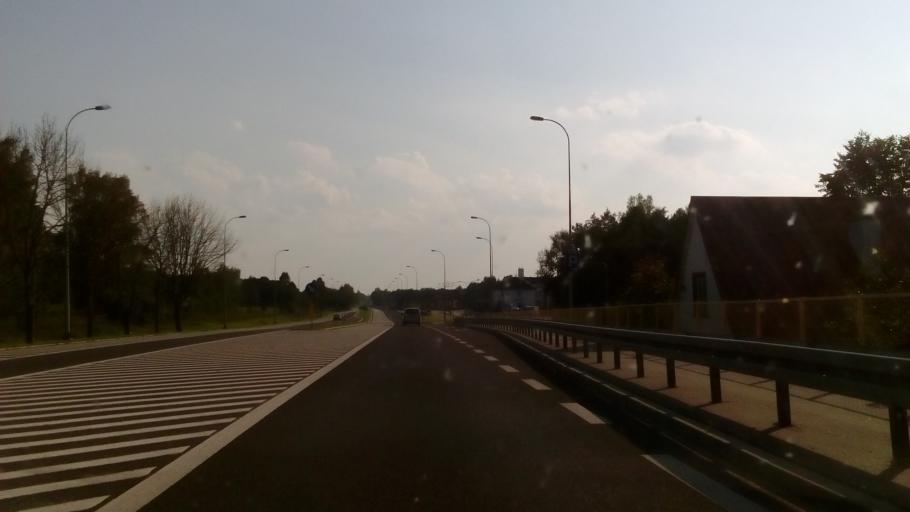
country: LT
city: Lazdijai
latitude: 54.1633
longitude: 23.4752
